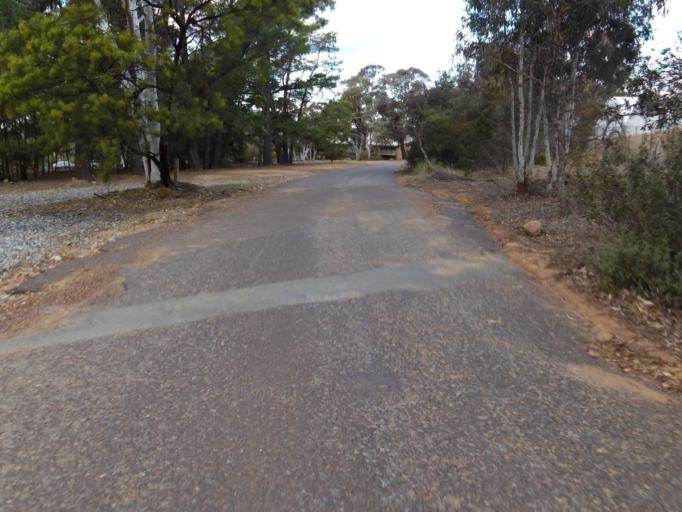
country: AU
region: Australian Capital Territory
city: Acton
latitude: -35.2705
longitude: 149.1092
